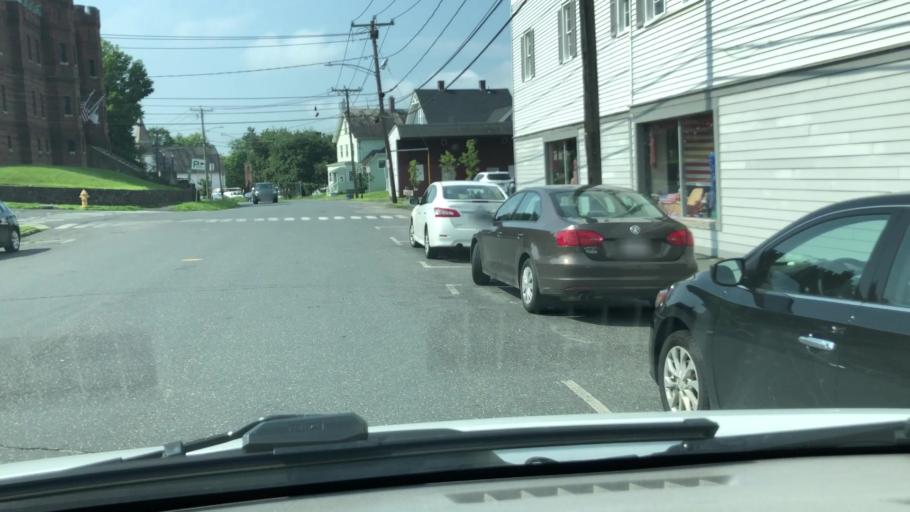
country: US
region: Massachusetts
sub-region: Franklin County
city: Greenfield
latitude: 42.5859
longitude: -72.5991
